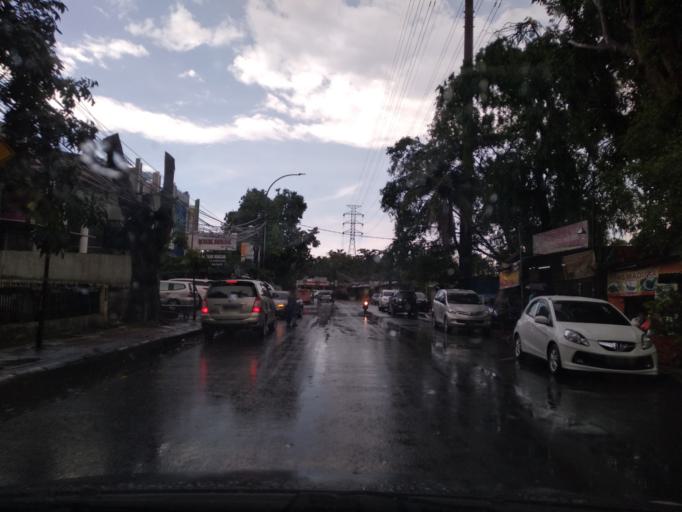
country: ID
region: Jakarta Raya
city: Jakarta
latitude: -6.2192
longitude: 106.8870
